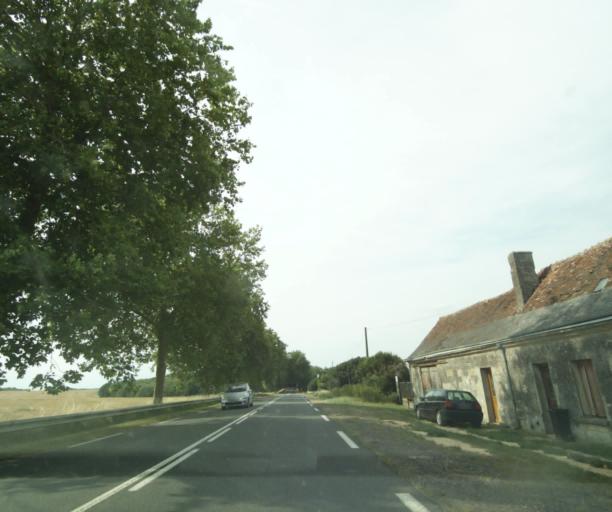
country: FR
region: Centre
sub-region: Departement d'Indre-et-Loire
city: Saint-Paterne-Racan
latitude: 47.6094
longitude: 0.5112
